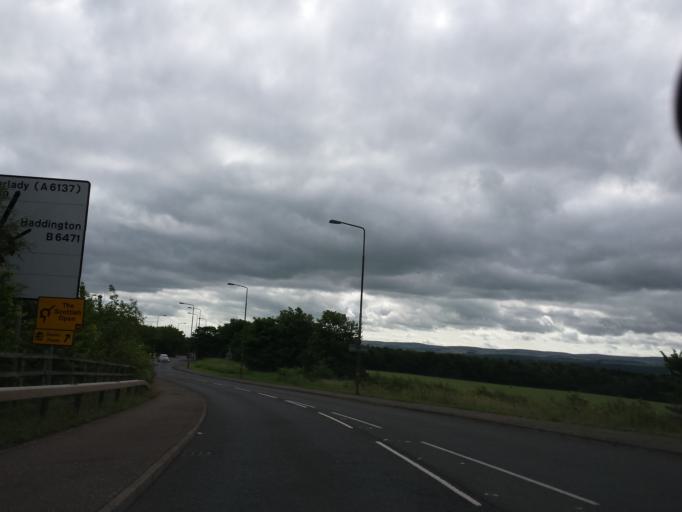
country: GB
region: Scotland
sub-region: East Lothian
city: Haddington
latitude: 55.9543
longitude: -2.8181
